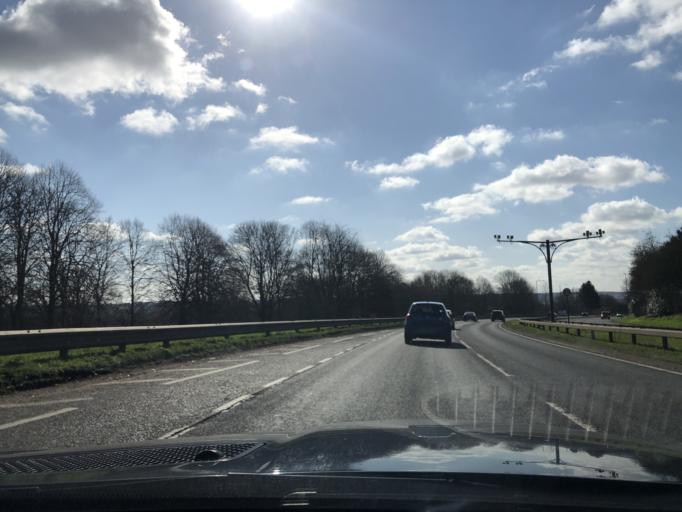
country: GB
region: England
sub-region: Northamptonshire
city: Northampton
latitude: 52.2530
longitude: -0.8346
